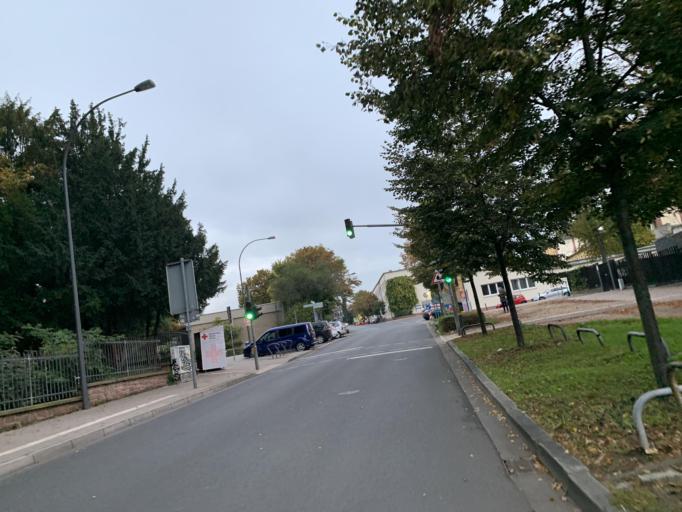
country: DE
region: Hesse
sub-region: Regierungsbezirk Darmstadt
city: Frankfurt am Main
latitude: 50.1309
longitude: 8.7055
